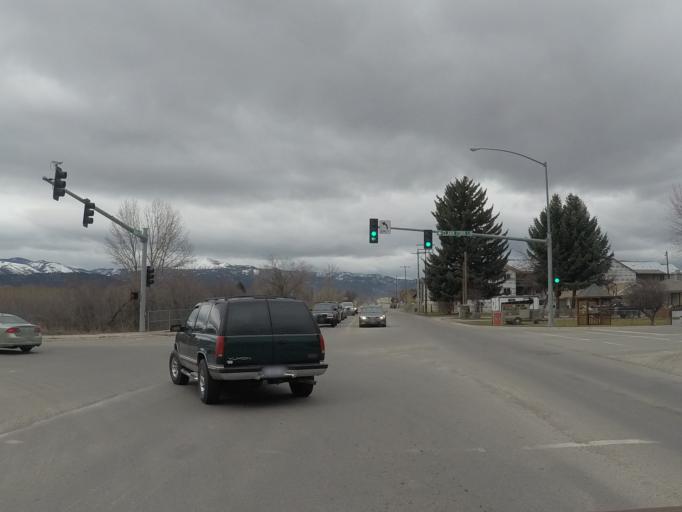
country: US
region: Montana
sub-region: Missoula County
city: Orchard Homes
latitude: 46.8855
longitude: -114.0438
